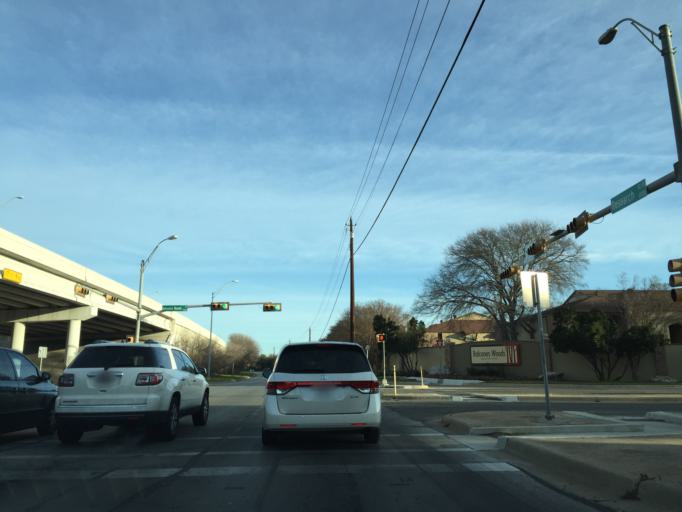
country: US
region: Texas
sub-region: Williamson County
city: Jollyville
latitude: 30.4076
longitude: -97.7447
